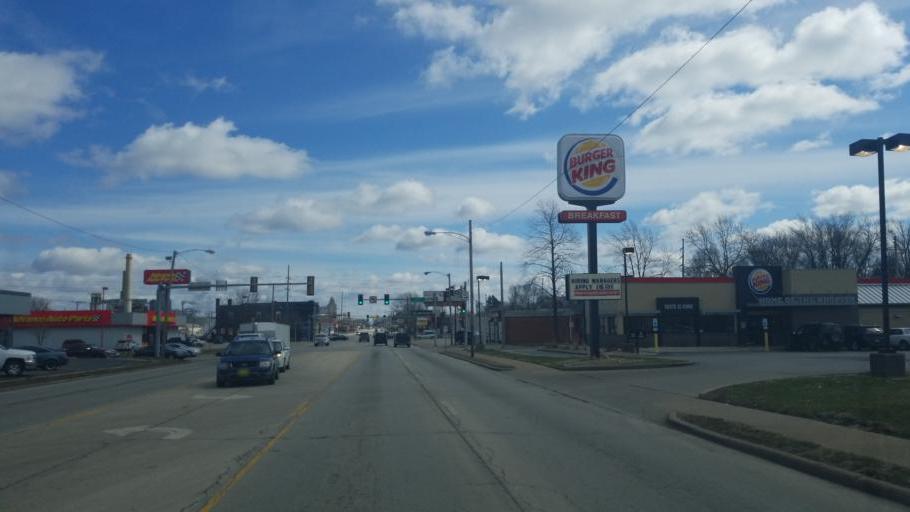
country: US
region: Illinois
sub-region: Macon County
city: Decatur
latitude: 39.8461
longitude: -88.9427
